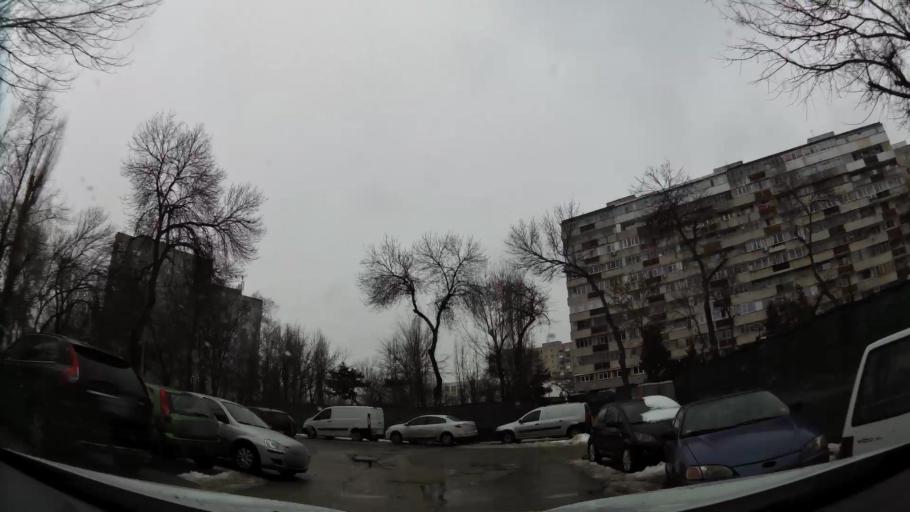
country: RO
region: Ilfov
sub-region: Comuna Chiajna
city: Rosu
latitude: 44.4142
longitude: 26.0253
